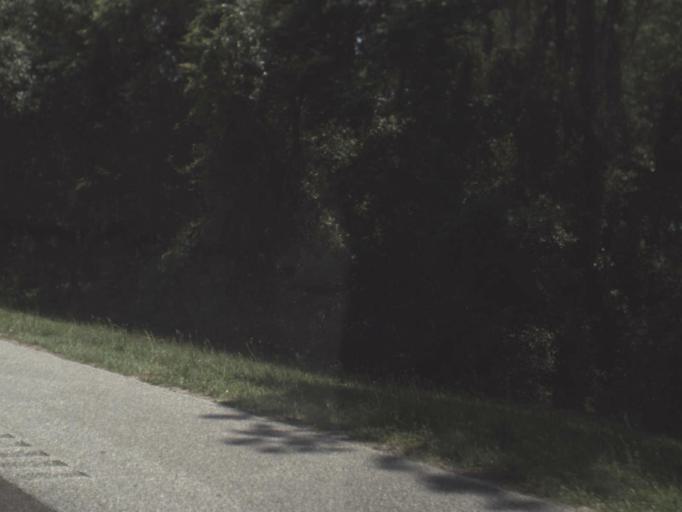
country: US
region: Florida
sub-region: Saint Johns County
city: Fruit Cove
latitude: 30.1742
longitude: -81.6177
